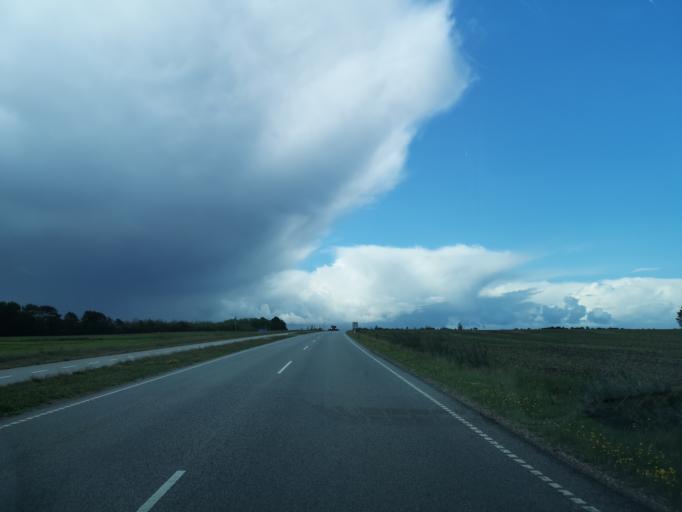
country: DK
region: Central Jutland
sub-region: Herning Kommune
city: Snejbjerg
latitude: 56.1230
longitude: 8.9151
